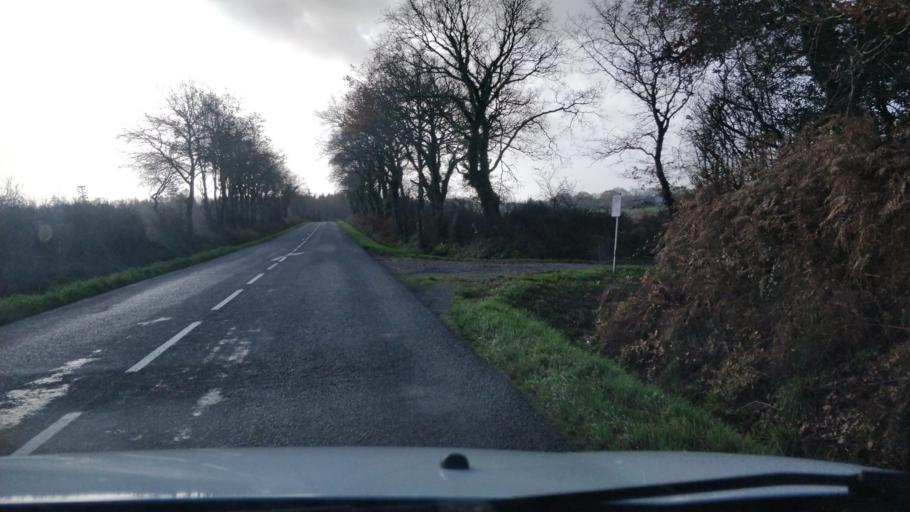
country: FR
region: Pays de la Loire
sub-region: Departement de la Loire-Atlantique
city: Saint-Molf
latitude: 47.3646
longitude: -2.4310
